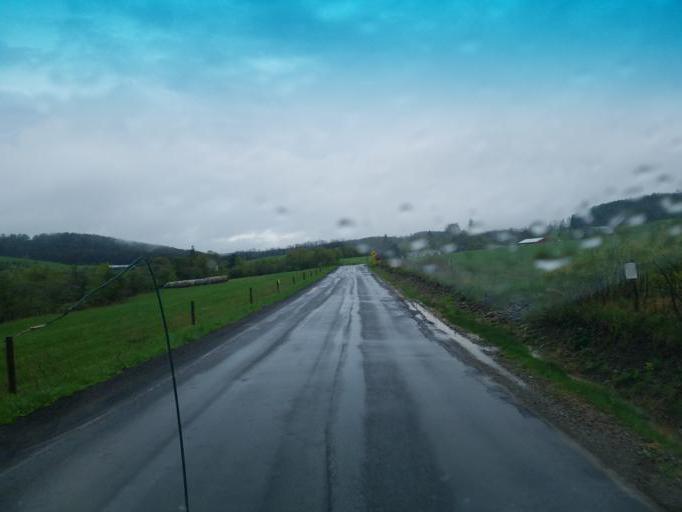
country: US
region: Pennsylvania
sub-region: Tioga County
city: Westfield
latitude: 41.9686
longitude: -77.6578
